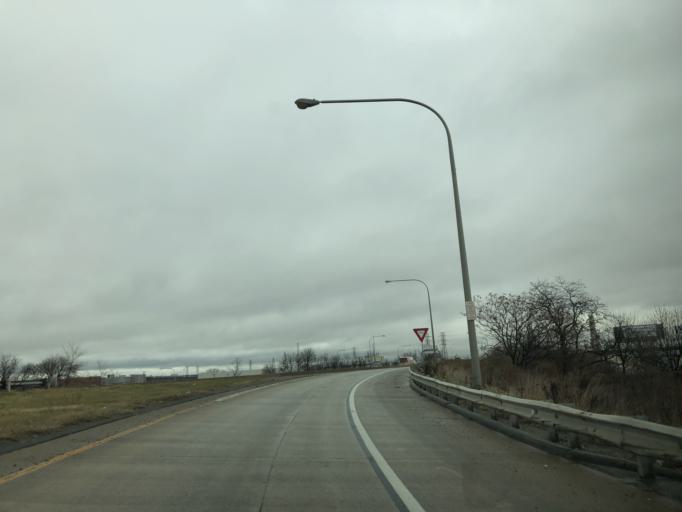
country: US
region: Delaware
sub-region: New Castle County
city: Wilmington
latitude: 39.7189
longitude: -75.5412
